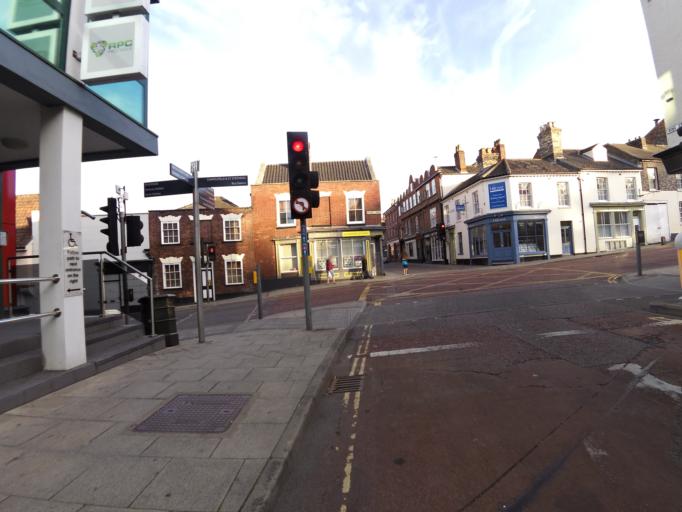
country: GB
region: England
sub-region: Norfolk
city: Norwich
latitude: 52.6284
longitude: 1.2995
